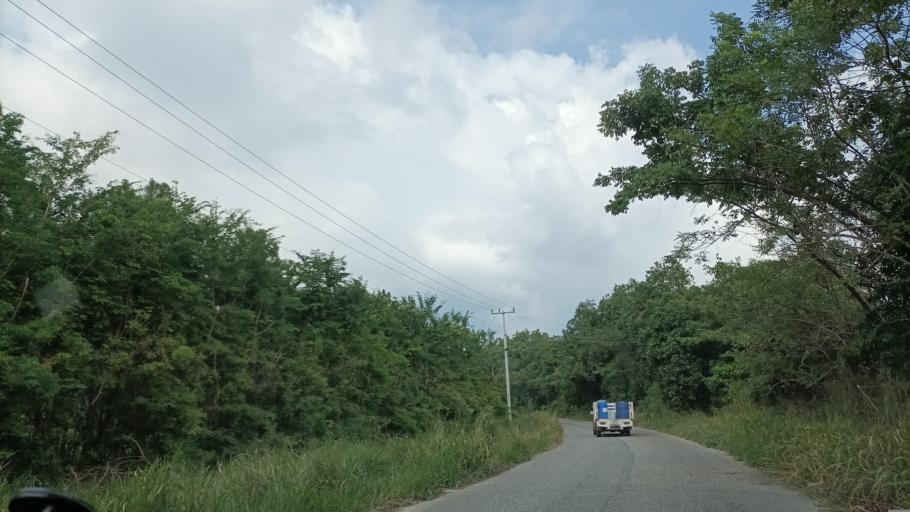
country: MX
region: Veracruz
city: Las Choapas
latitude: 17.8031
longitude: -94.1080
